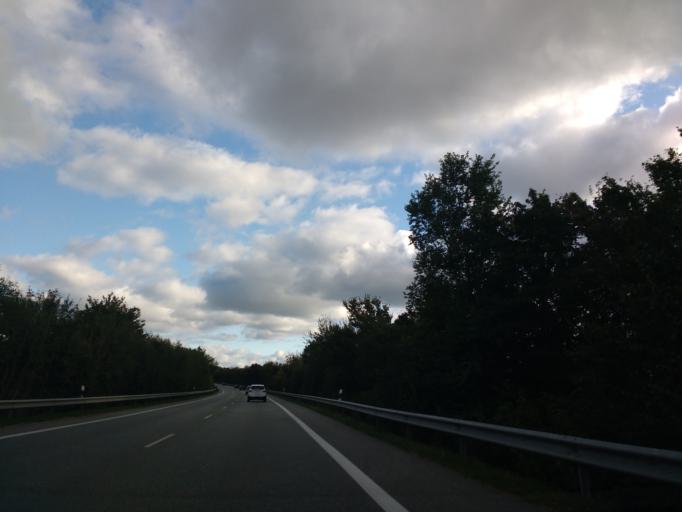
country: DE
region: Schleswig-Holstein
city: Altenkrempe
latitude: 54.1246
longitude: 10.8295
